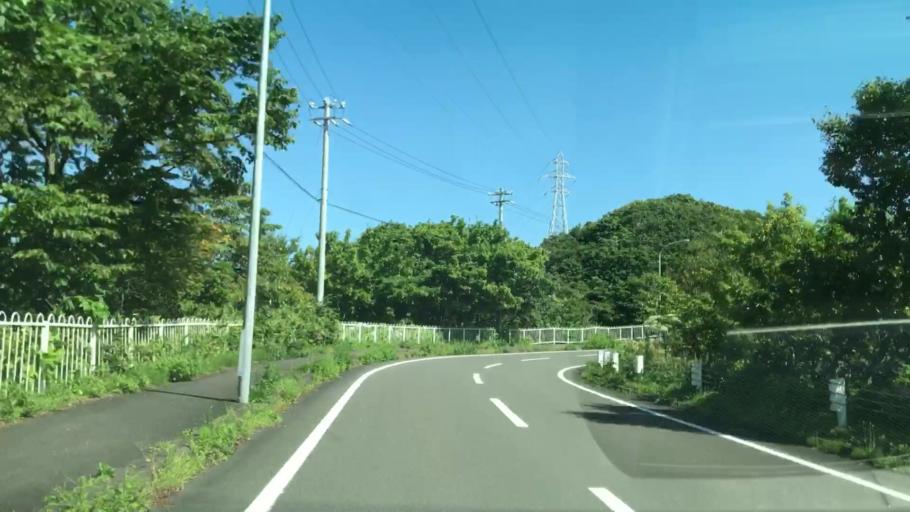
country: JP
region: Hokkaido
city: Muroran
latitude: 42.3043
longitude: 140.9996
